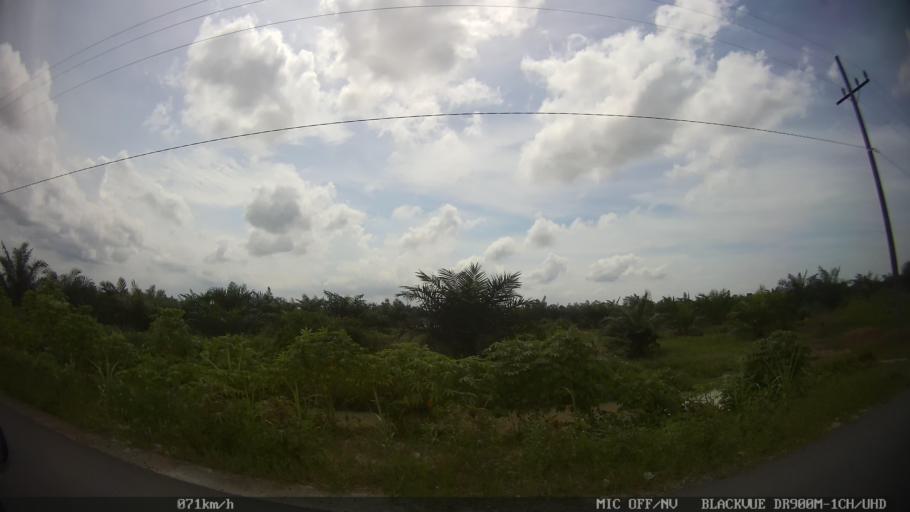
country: ID
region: North Sumatra
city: Percut
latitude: 3.5787
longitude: 98.8407
